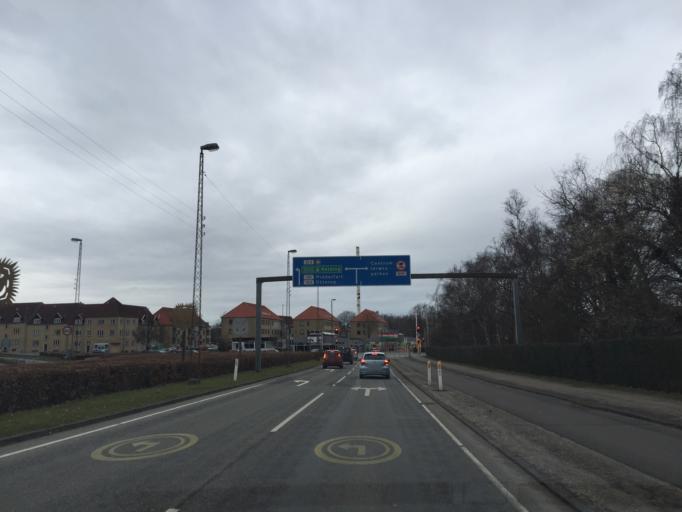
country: DK
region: South Denmark
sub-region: Odense Kommune
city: Odense
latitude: 55.3925
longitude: 10.3463
